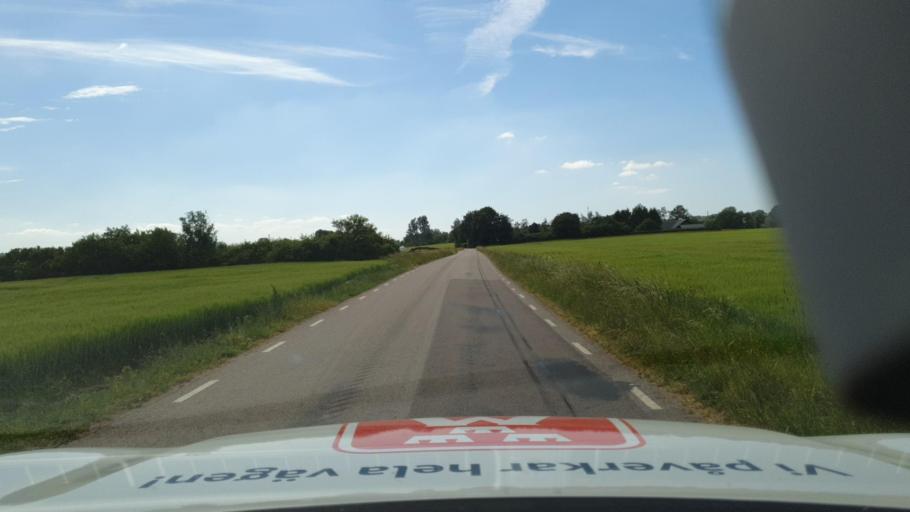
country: SE
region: Skane
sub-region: Sjobo Kommun
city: Sjoebo
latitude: 55.6383
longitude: 13.7919
